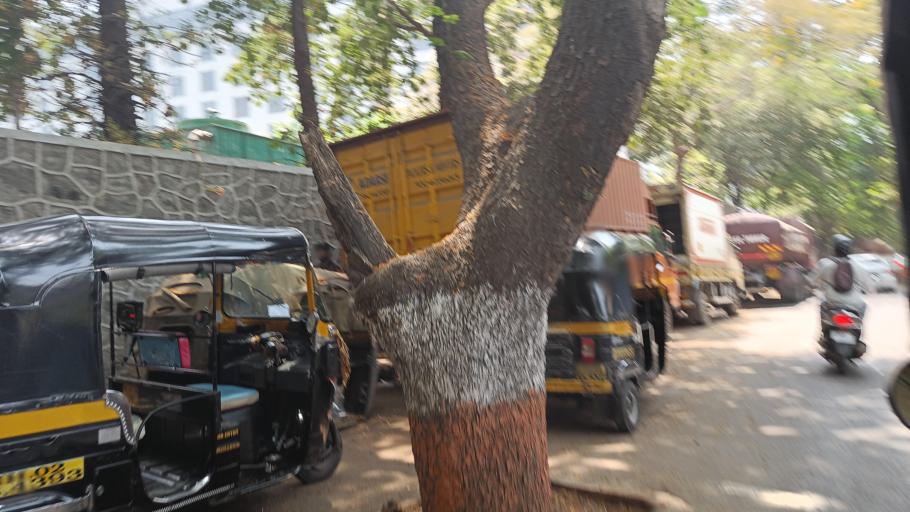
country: IN
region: Maharashtra
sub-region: Mumbai Suburban
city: Mumbai
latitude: 19.0787
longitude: 72.8513
